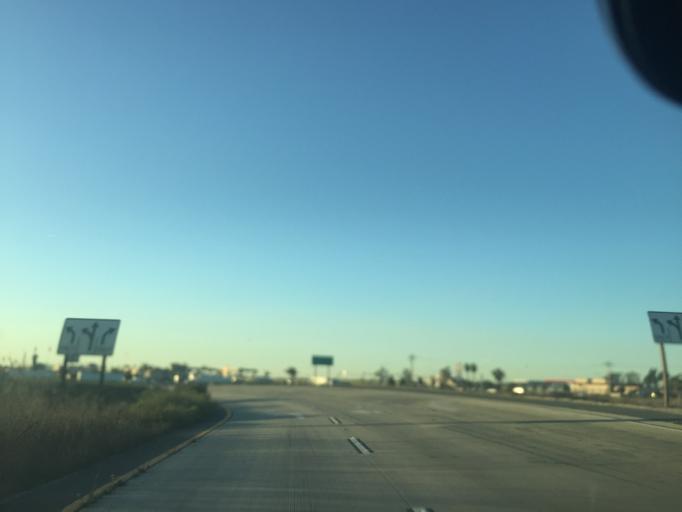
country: MX
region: Baja California
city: Tijuana
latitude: 32.5657
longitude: -116.9600
